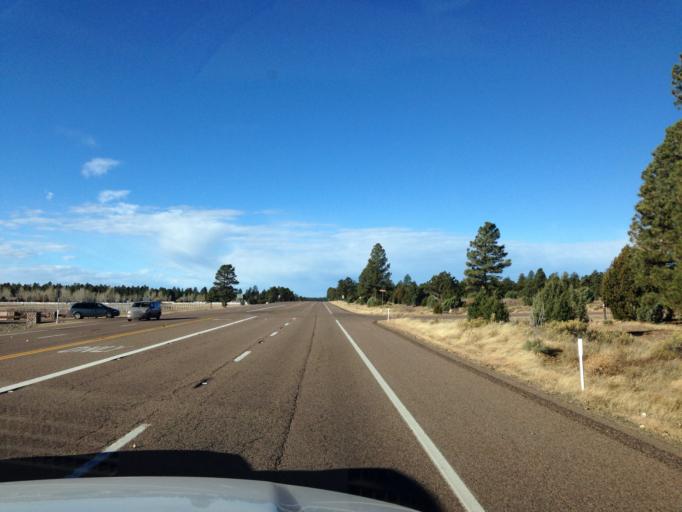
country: US
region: Arizona
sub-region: Navajo County
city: Heber-Overgaard
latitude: 34.3929
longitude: -110.5268
